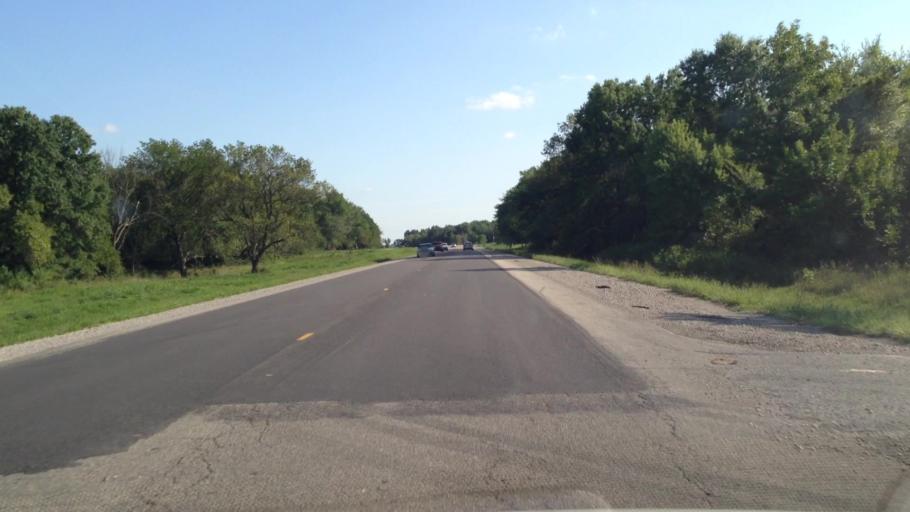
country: US
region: Kansas
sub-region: Crawford County
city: Arma
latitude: 37.5285
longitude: -94.7112
